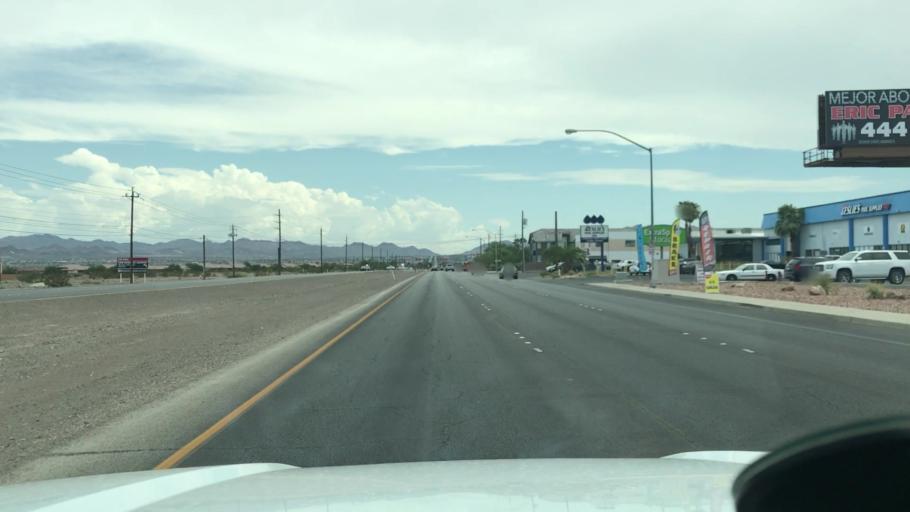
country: US
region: Nevada
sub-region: Clark County
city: Whitney
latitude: 36.0792
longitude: -115.0268
